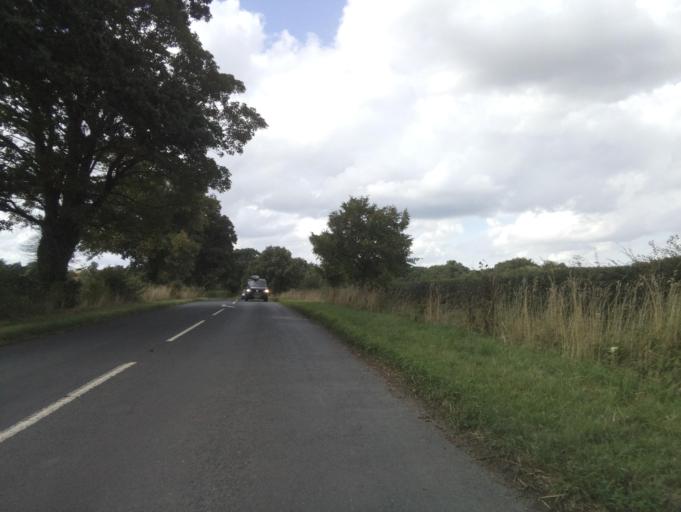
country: GB
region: England
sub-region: North Yorkshire
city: Bedale
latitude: 54.2017
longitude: -1.5838
